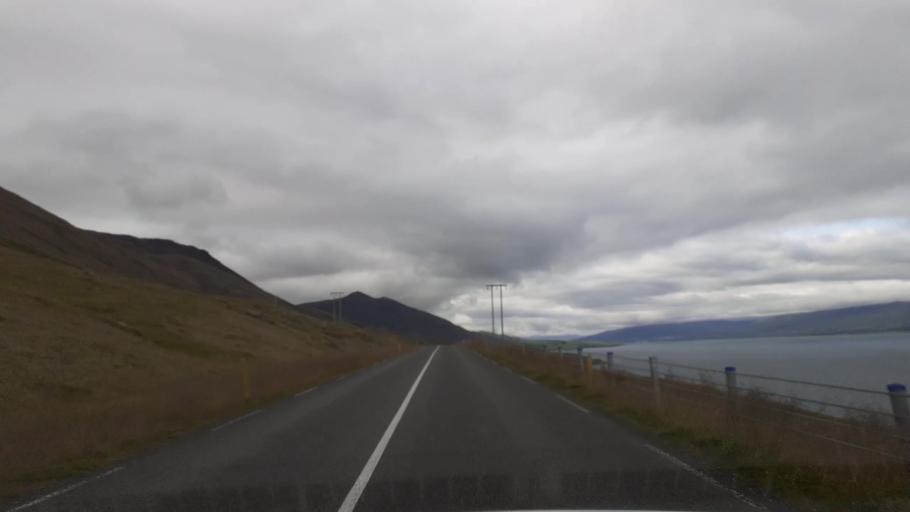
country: IS
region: Northeast
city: Akureyri
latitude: 65.8537
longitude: -18.0610
